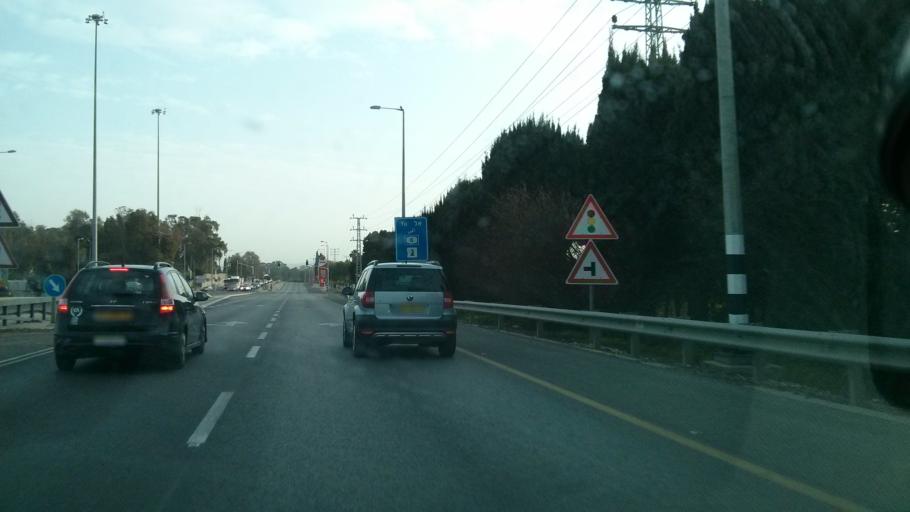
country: IL
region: Central District
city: Elyakhin
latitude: 32.4577
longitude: 34.9846
